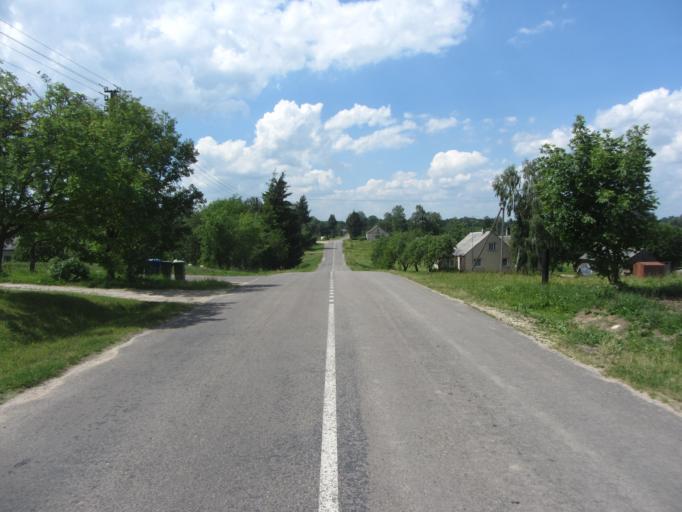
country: LT
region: Alytaus apskritis
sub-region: Alytus
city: Alytus
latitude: 54.4484
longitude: 24.1285
